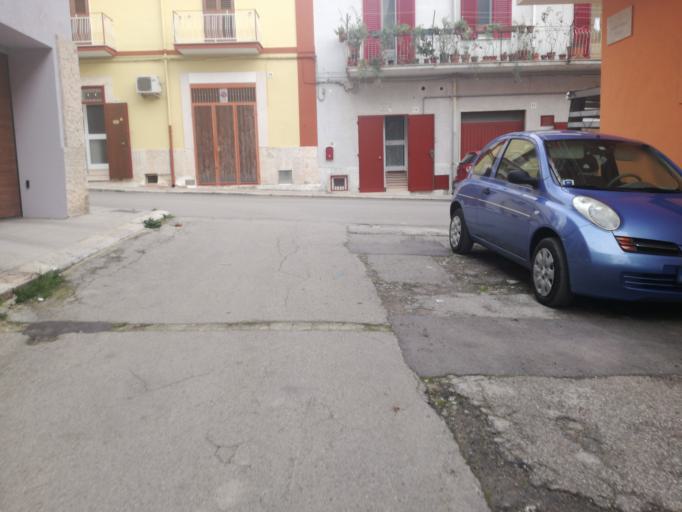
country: IT
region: Apulia
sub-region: Provincia di Bari
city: Ruvo di Puglia
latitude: 41.1182
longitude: 16.4801
